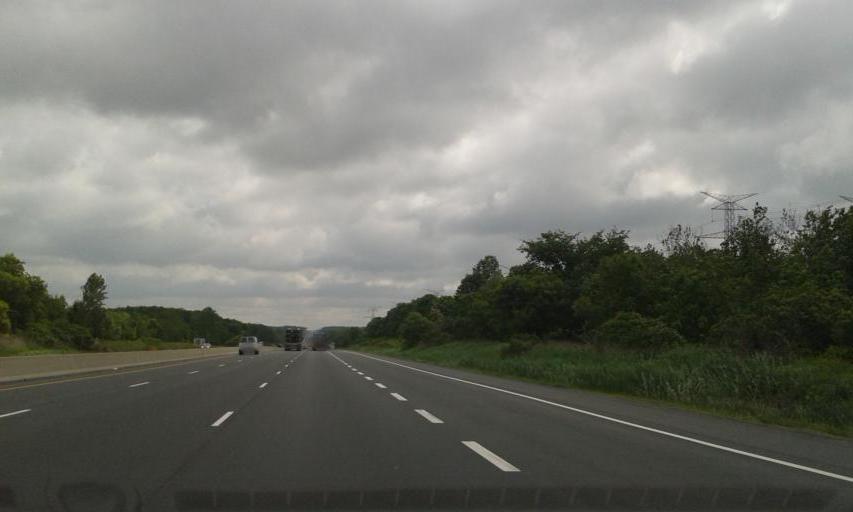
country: CA
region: Ontario
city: Cobourg
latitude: 43.9321
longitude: -78.4838
